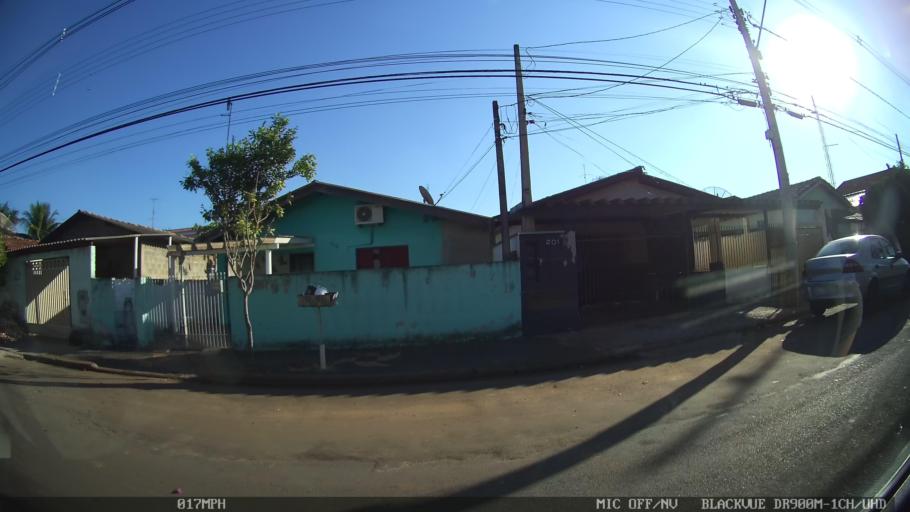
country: BR
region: Sao Paulo
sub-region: Nova Odessa
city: Nova Odessa
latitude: -22.7711
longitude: -47.2901
